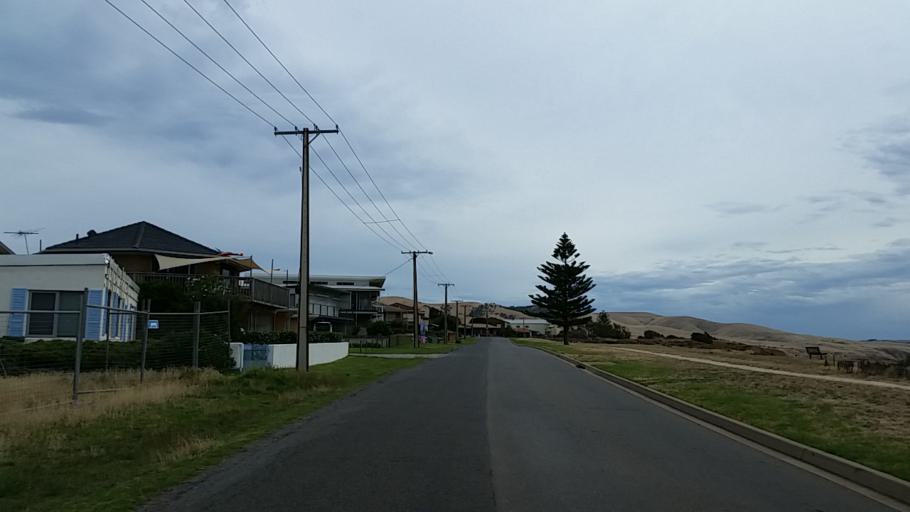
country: AU
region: South Australia
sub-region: Onkaparinga
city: Port Willunga
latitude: -35.3372
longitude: 138.4476
